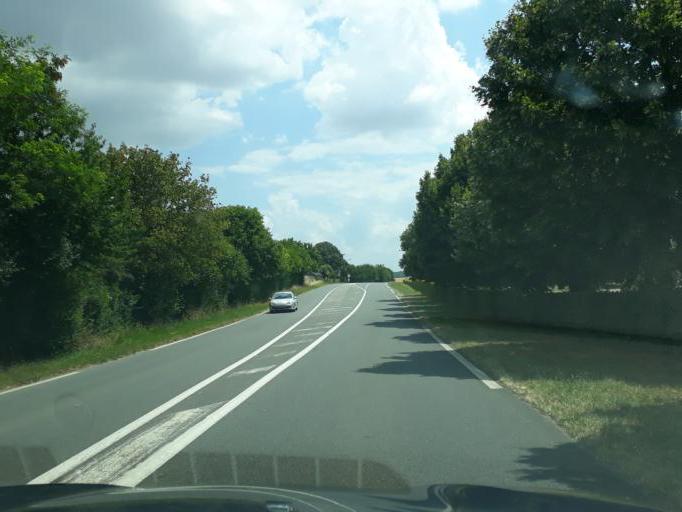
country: FR
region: Centre
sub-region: Departement du Cher
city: Avord
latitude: 47.0311
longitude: 2.6499
